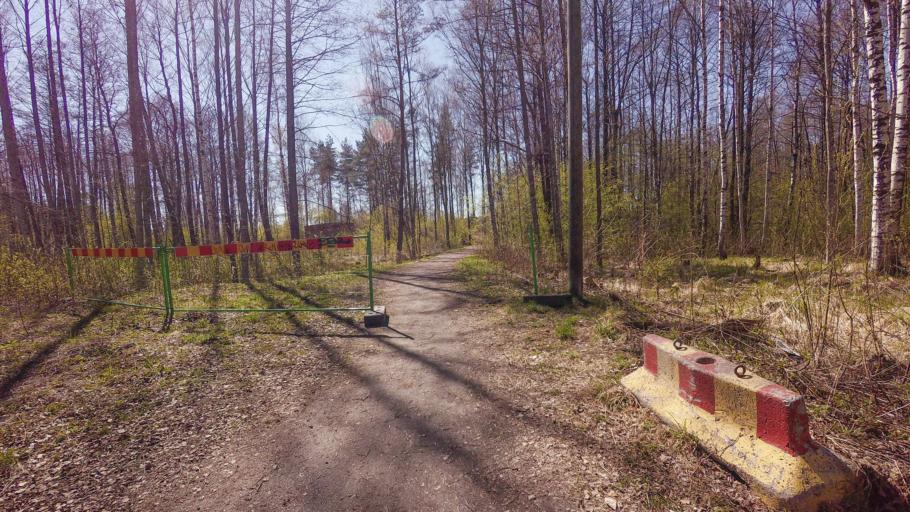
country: FI
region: Uusimaa
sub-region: Helsinki
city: Vantaa
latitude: 60.2234
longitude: 25.1304
